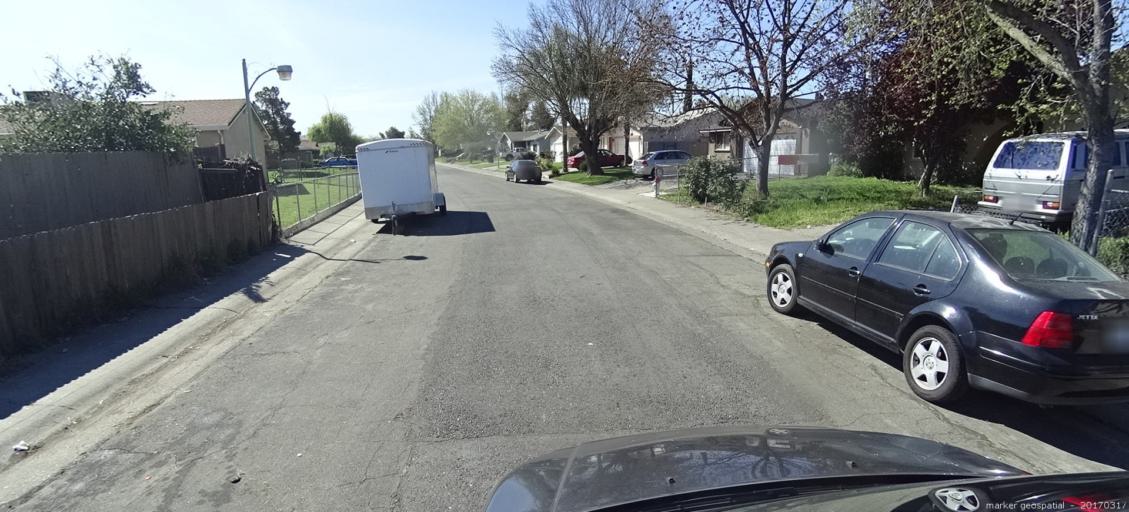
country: US
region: California
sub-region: Sacramento County
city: Parkway
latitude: 38.4872
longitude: -121.4915
